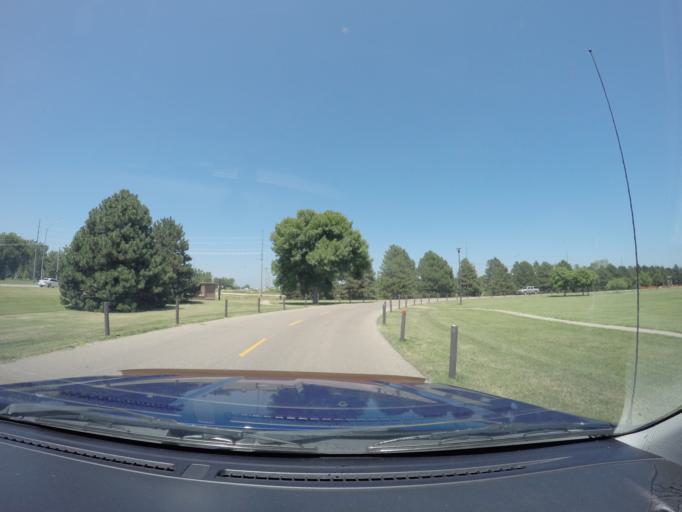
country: US
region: Nebraska
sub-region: Phelps County
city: Holdrege
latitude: 40.4517
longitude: -99.3787
